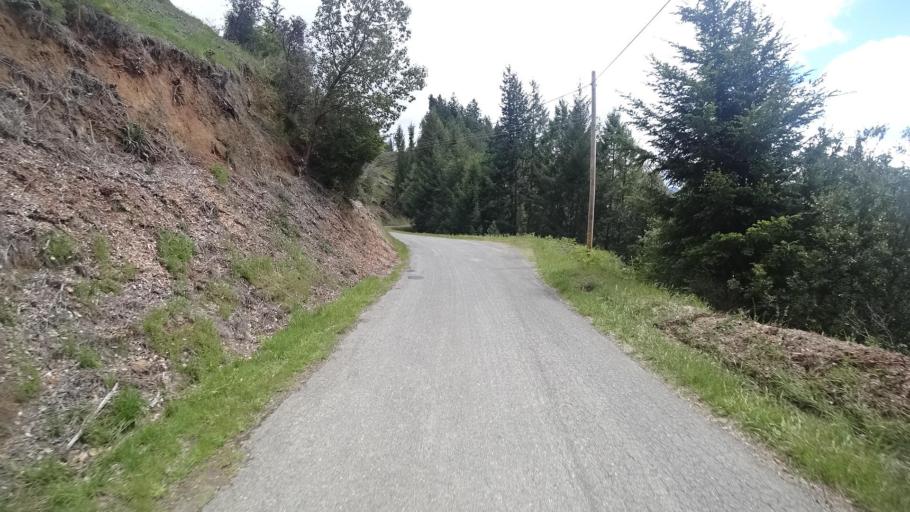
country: US
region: California
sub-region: Humboldt County
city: Blue Lake
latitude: 40.7670
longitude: -123.9298
